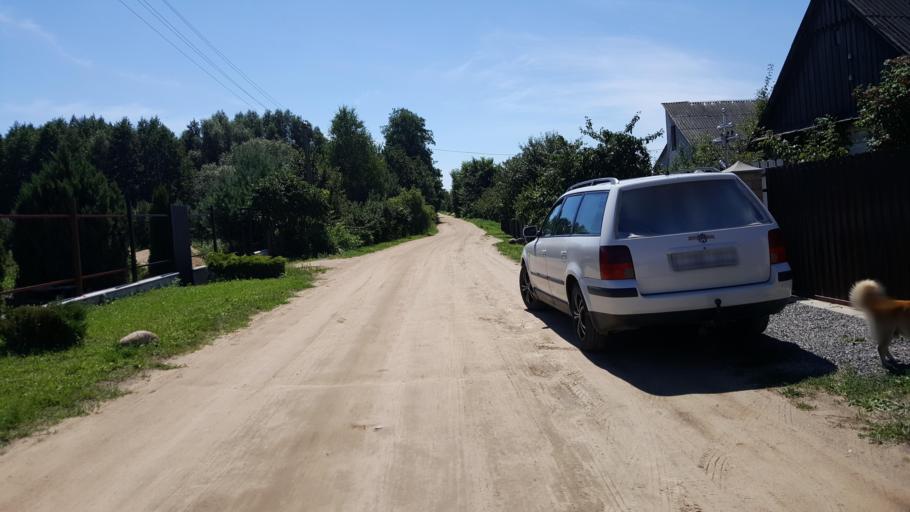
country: BY
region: Brest
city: Charnawchytsy
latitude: 52.2289
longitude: 23.7798
